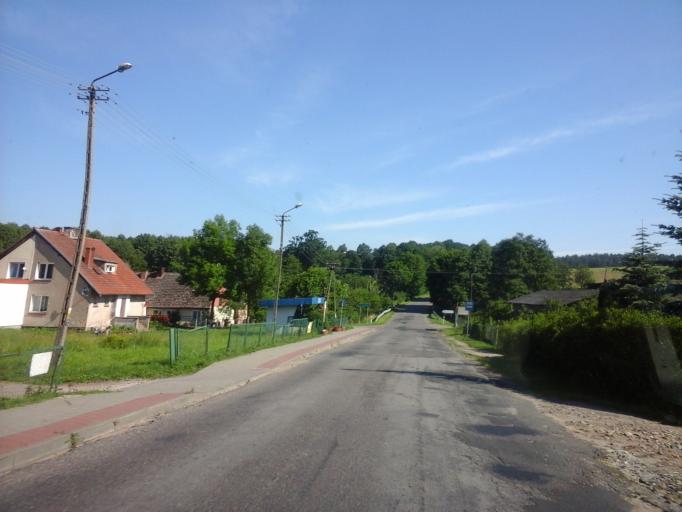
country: PL
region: West Pomeranian Voivodeship
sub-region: Powiat swidwinski
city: Polczyn-Zdroj
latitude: 53.6739
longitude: 16.0180
